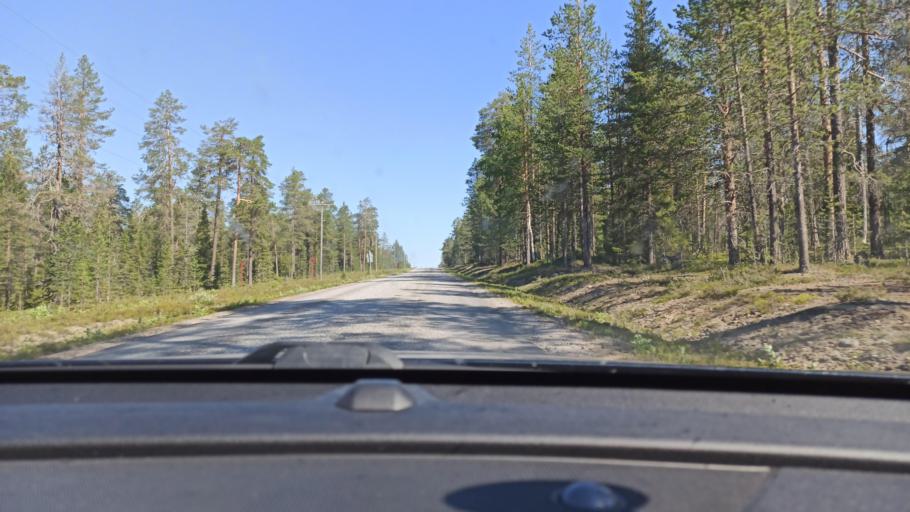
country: FI
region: Lapland
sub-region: Tunturi-Lappi
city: Kolari
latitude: 67.6385
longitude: 24.1568
